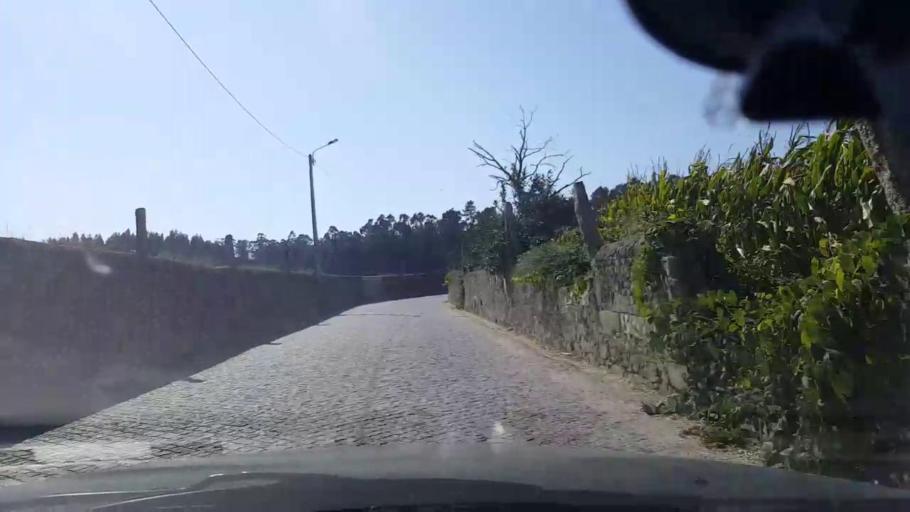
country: PT
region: Porto
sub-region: Povoa de Varzim
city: Pedroso
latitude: 41.4018
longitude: -8.6919
